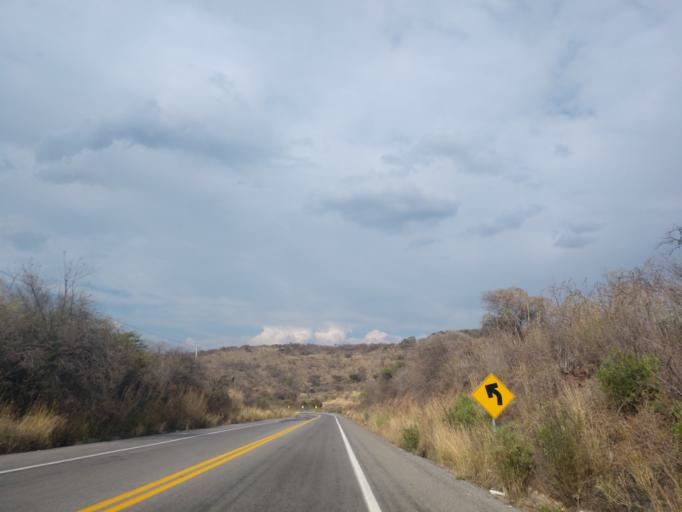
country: MX
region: Jalisco
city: La Manzanilla de la Paz
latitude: 20.0814
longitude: -103.1669
